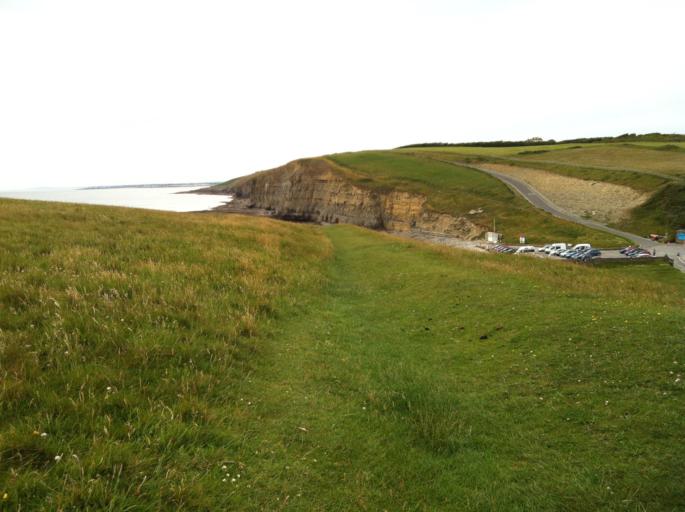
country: GB
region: Wales
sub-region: Bridgend county borough
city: Merthyr Mawr
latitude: 51.4448
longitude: -3.6045
